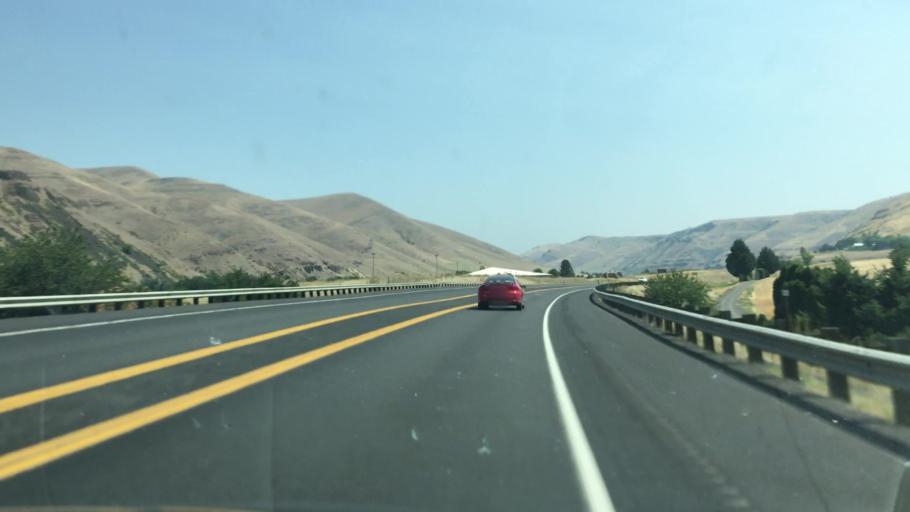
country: US
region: Idaho
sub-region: Nez Perce County
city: Lapwai
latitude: 46.4456
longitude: -116.8278
